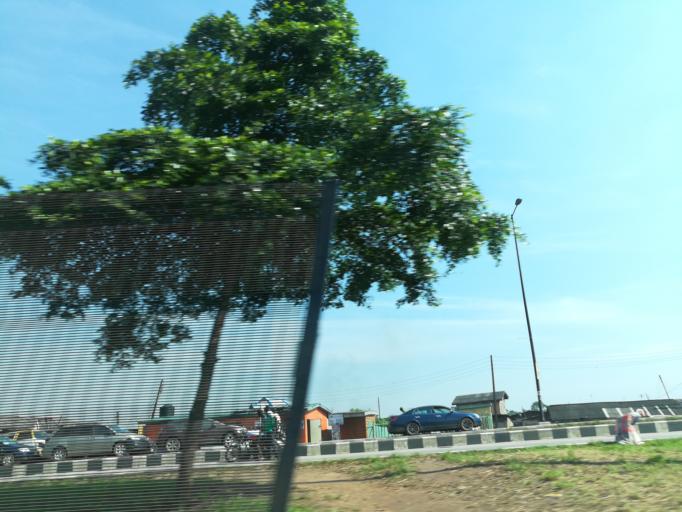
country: NG
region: Lagos
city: Ojota
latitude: 6.6121
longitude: 3.4162
